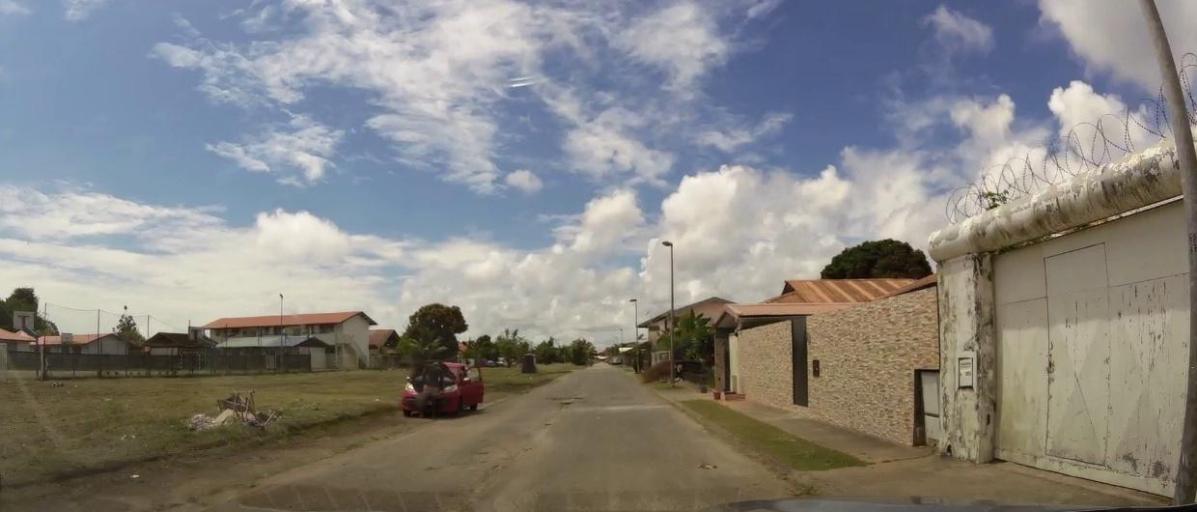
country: GF
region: Guyane
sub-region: Guyane
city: Kourou
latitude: 5.1707
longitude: -52.6562
